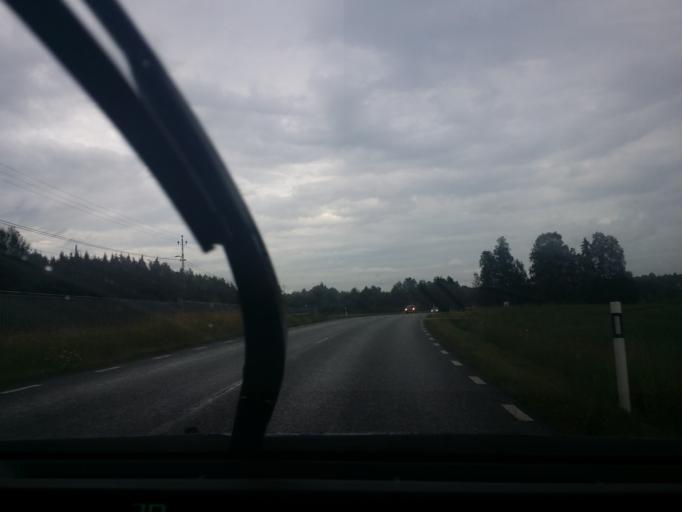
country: SE
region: OErebro
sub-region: Lindesbergs Kommun
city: Frovi
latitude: 59.4663
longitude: 15.3310
